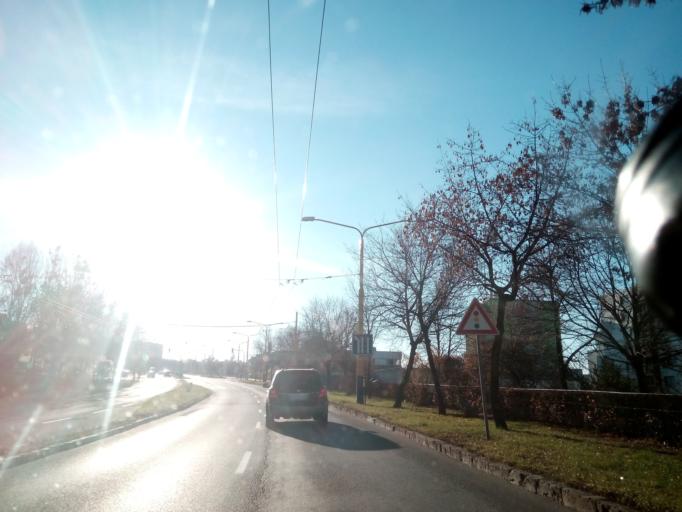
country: SK
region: Kosicky
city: Kosice
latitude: 48.7397
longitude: 21.2811
